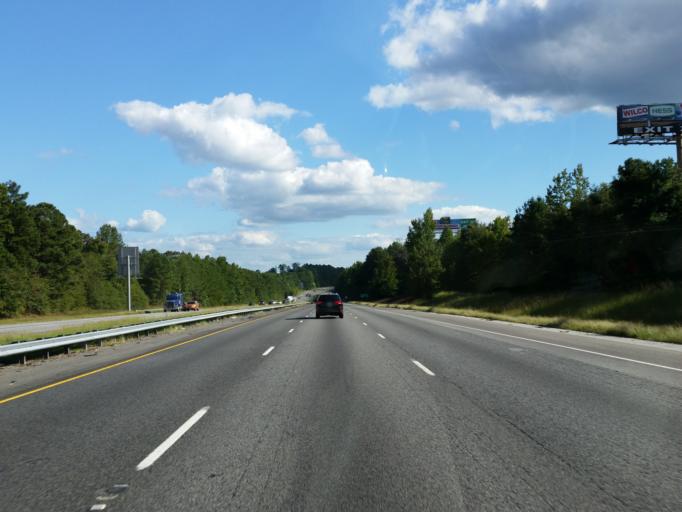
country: US
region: Georgia
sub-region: Henry County
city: Locust Grove
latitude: 33.2529
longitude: -84.0896
